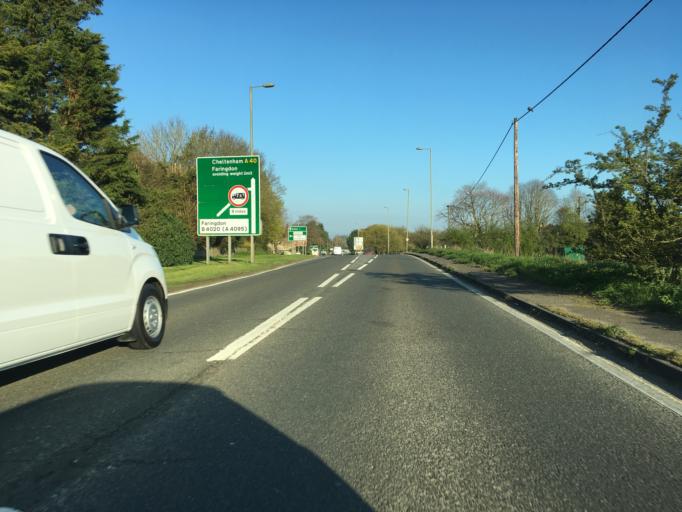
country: GB
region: England
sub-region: Oxfordshire
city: Burford
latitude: 51.8011
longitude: -1.6308
